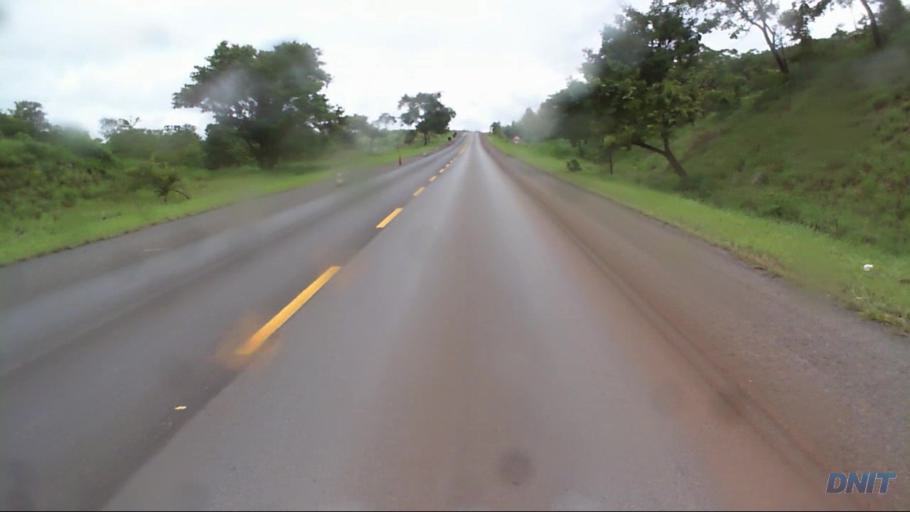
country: BR
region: Goias
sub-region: Padre Bernardo
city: Padre Bernardo
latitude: -15.1858
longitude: -48.4321
